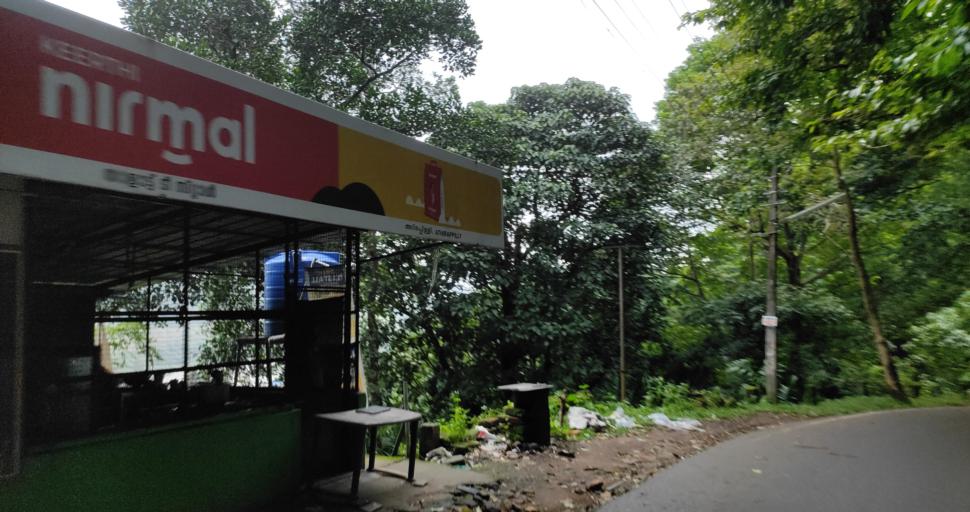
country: IN
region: Kerala
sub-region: Ernakulam
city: Angamali
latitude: 10.2884
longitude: 76.5643
